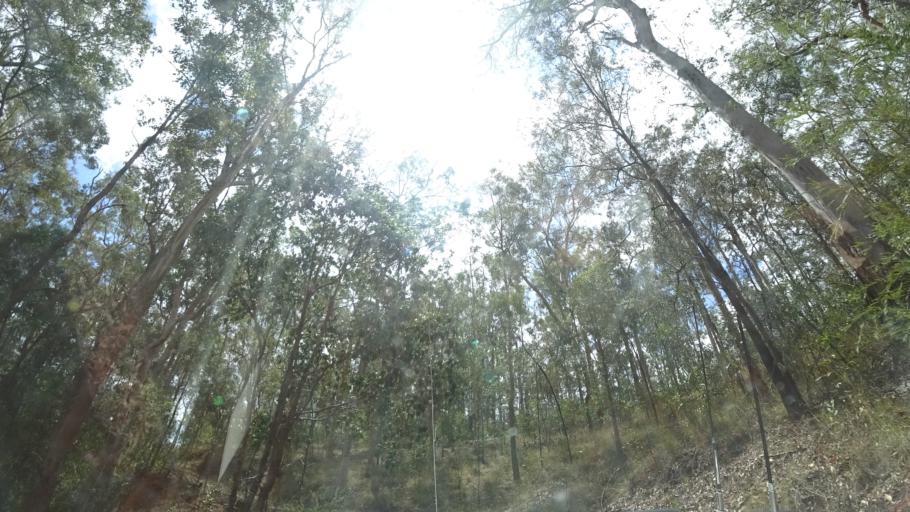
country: AU
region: Queensland
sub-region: Moreton Bay
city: Highvale
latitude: -27.4059
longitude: 152.7408
